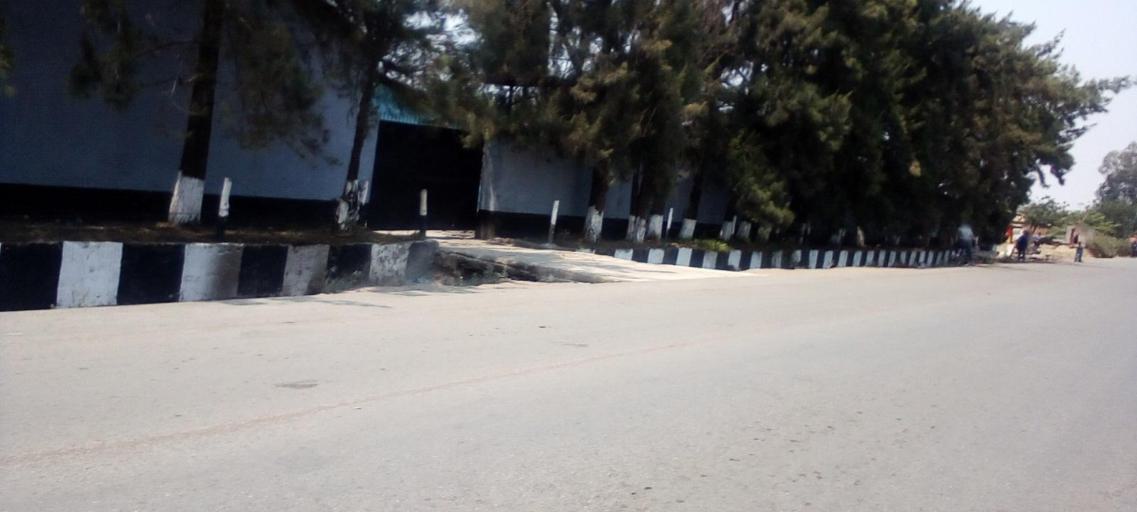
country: ZM
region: Lusaka
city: Lusaka
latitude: -15.4379
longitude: 28.2562
